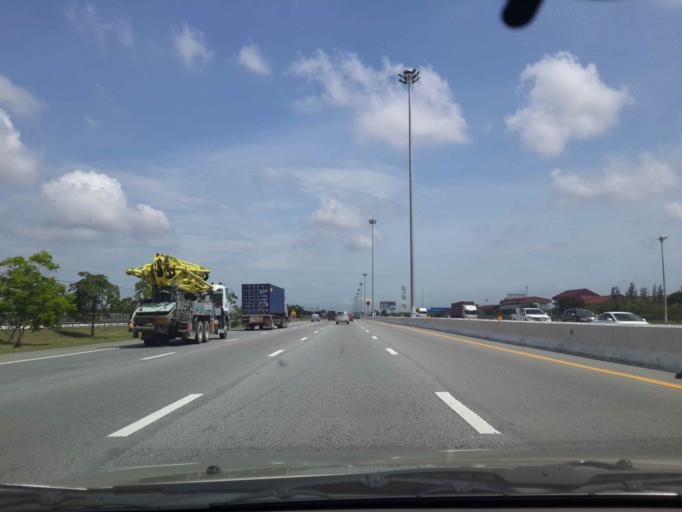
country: TH
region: Chachoengsao
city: Bang Pakong
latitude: 13.6002
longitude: 100.9524
